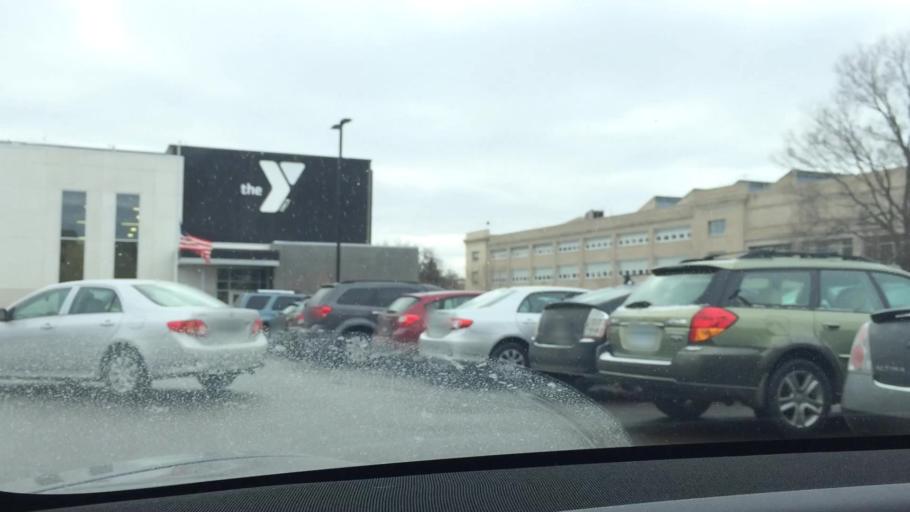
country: US
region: Minnesota
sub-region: Ramsey County
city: Falcon Heights
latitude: 44.9572
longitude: -93.1751
